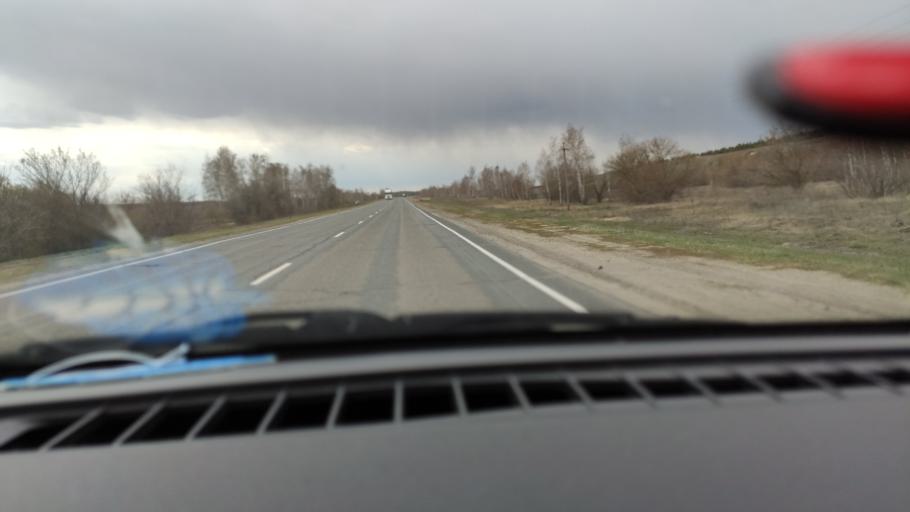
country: RU
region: Saratov
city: Sinodskoye
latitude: 52.0594
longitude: 46.7621
